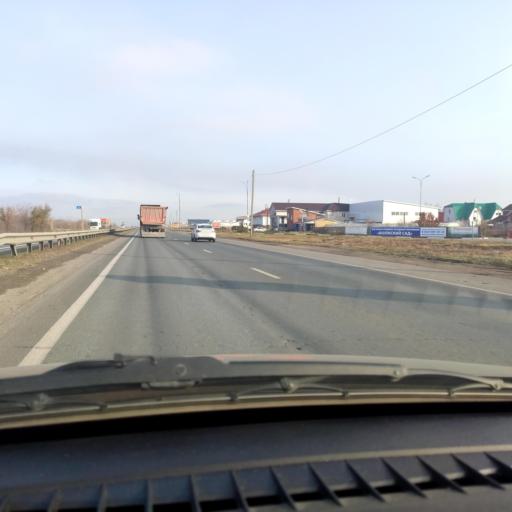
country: RU
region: Samara
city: Tol'yatti
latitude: 53.5646
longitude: 49.3651
